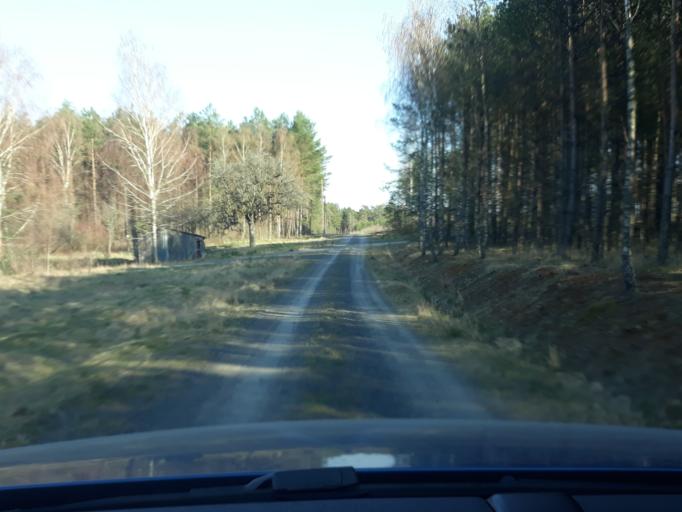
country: PL
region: Pomeranian Voivodeship
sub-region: Powiat bytowski
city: Lipnica
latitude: 53.9124
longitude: 17.4963
